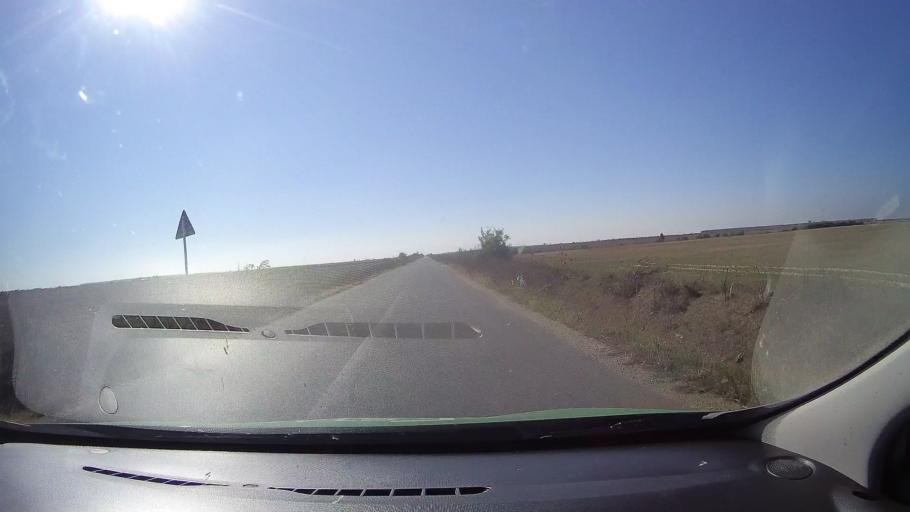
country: RO
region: Satu Mare
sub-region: Municipiul Satu Mare
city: Satmarel
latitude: 47.6991
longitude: 22.7690
